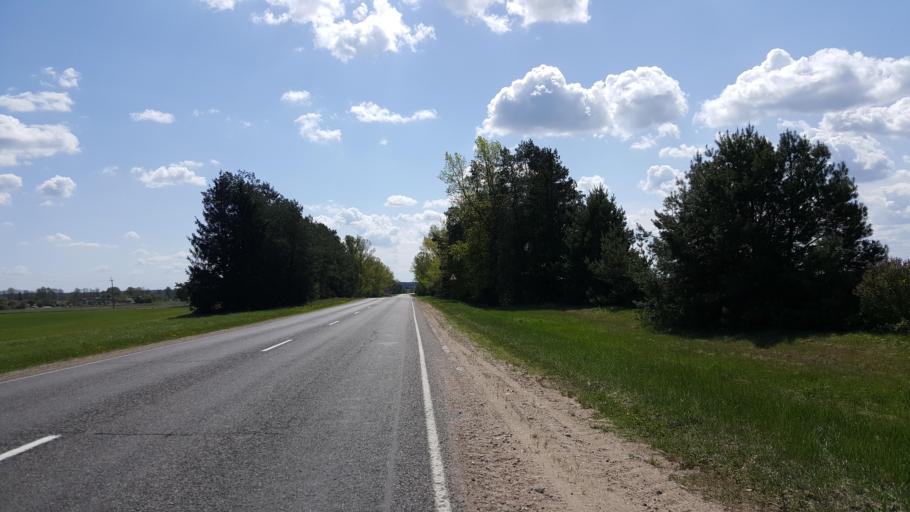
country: BY
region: Brest
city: Kamyanyets
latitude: 52.3756
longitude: 23.8749
